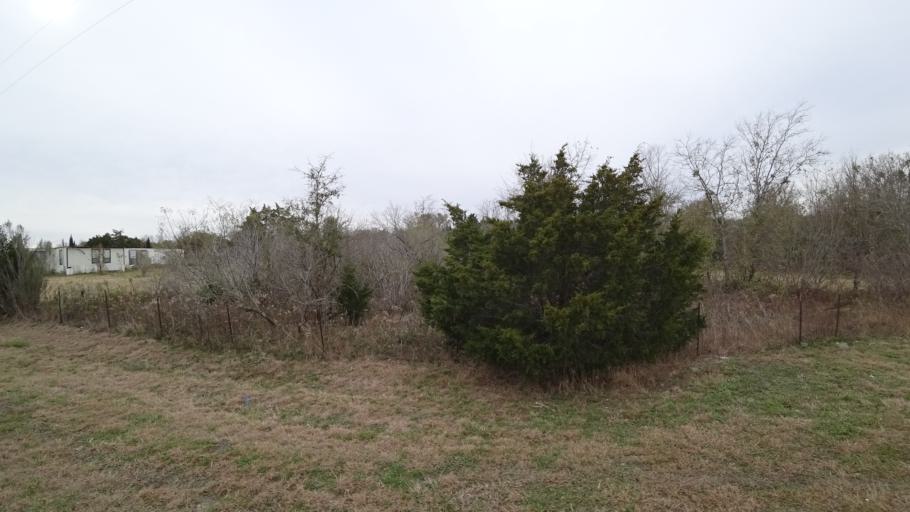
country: US
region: Texas
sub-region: Travis County
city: Garfield
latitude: 30.1110
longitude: -97.5885
